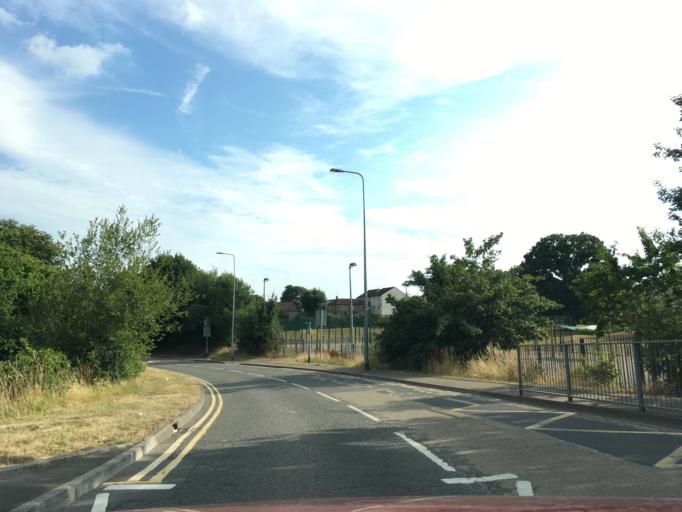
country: GB
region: Wales
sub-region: Newport
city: Marshfield
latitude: 51.5241
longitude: -3.1071
